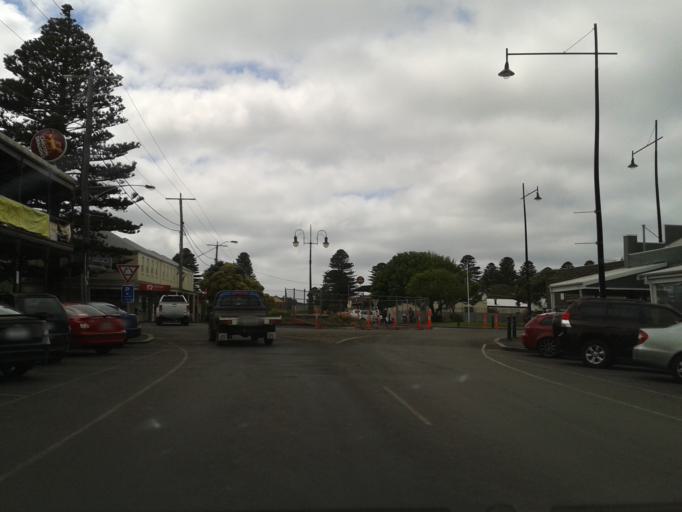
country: AU
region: Victoria
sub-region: Moyne
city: Port Fairy
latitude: -38.3834
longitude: 142.2365
